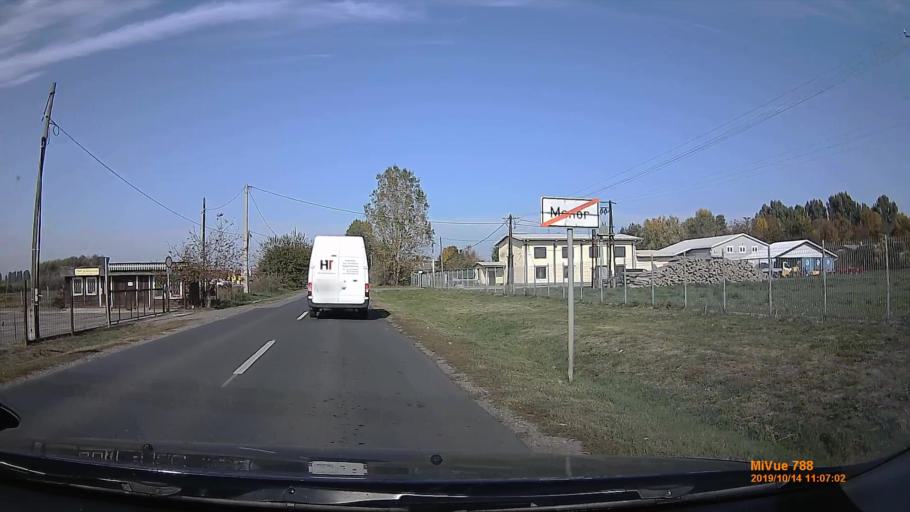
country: HU
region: Pest
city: Monor
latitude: 47.3634
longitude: 19.4299
